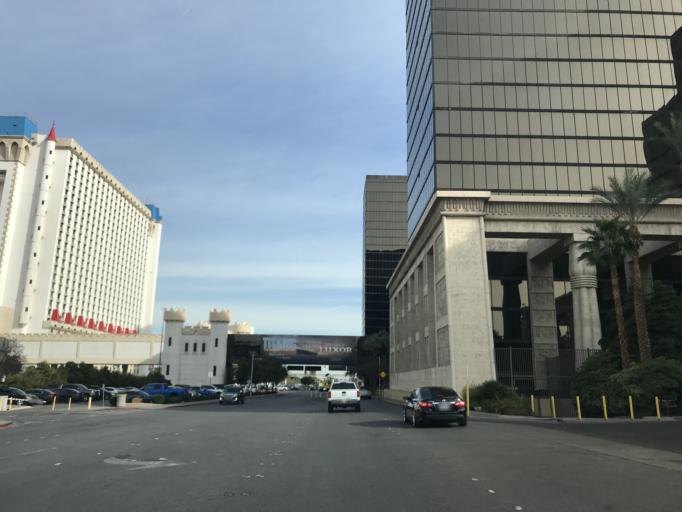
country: US
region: Nevada
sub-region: Clark County
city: Paradise
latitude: 36.0973
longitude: -115.1773
